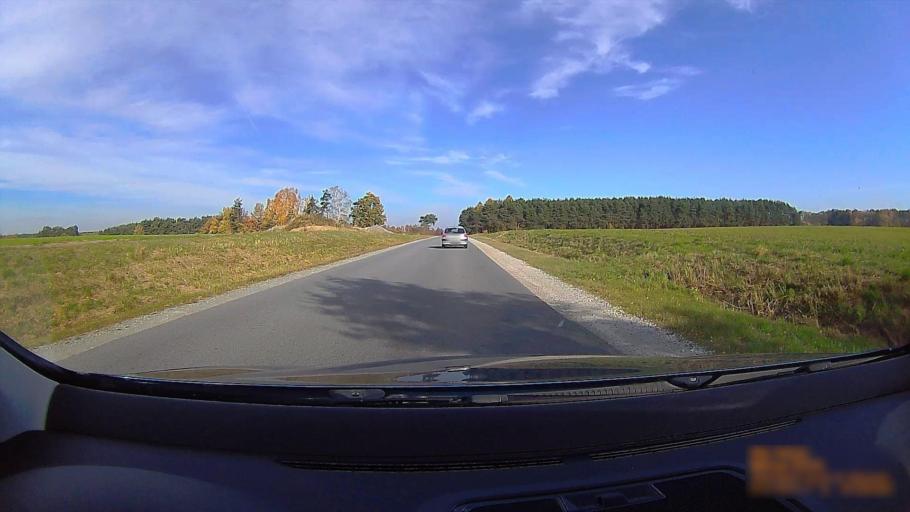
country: PL
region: Greater Poland Voivodeship
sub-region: Powiat ostrzeszowski
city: Doruchow
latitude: 51.3717
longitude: 18.0355
